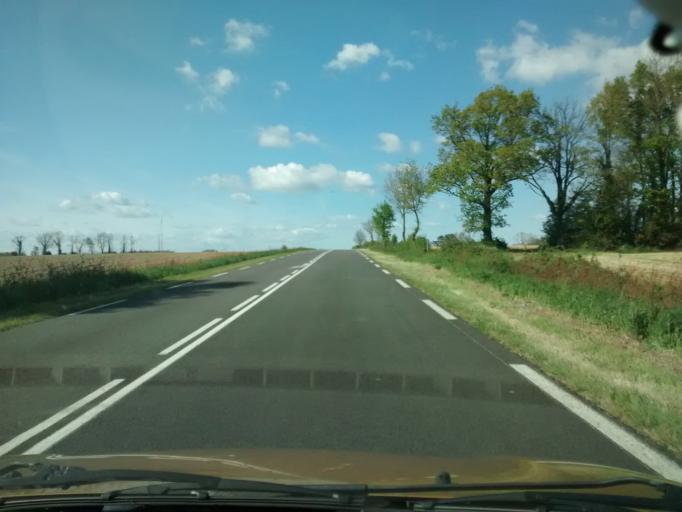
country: FR
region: Pays de la Loire
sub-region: Departement de la Vendee
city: Les Lucs-sur-Boulogne
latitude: 46.8698
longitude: -1.4992
